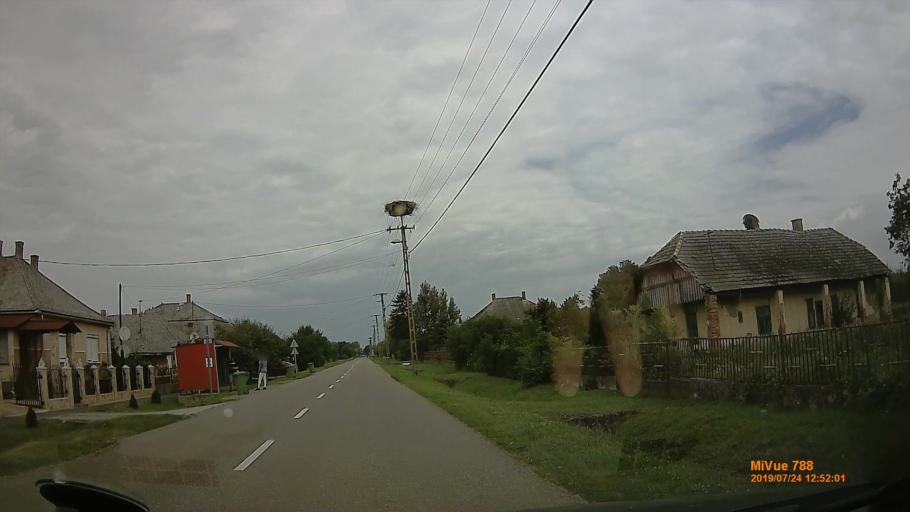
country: HU
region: Szabolcs-Szatmar-Bereg
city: Aranyosapati
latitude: 48.1954
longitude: 22.2956
